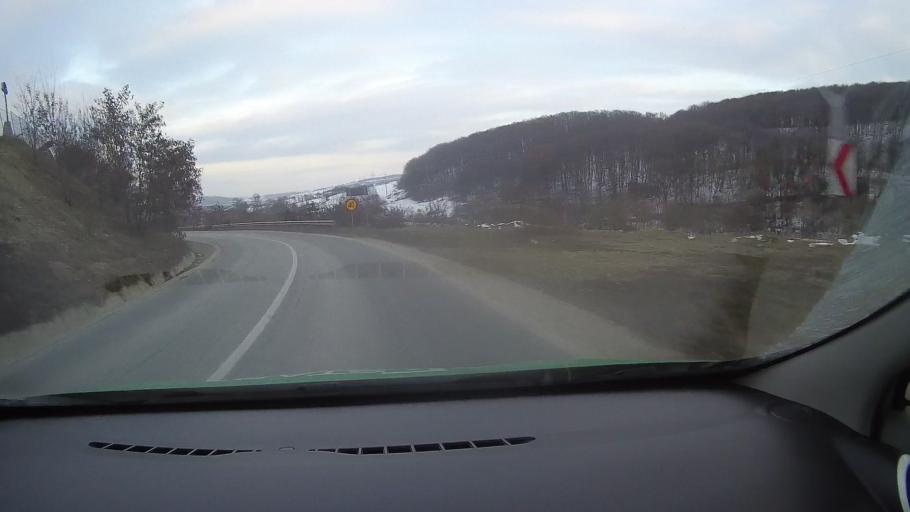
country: RO
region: Harghita
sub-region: Comuna Lupeni
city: Lupeni
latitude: 46.3575
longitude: 25.1931
